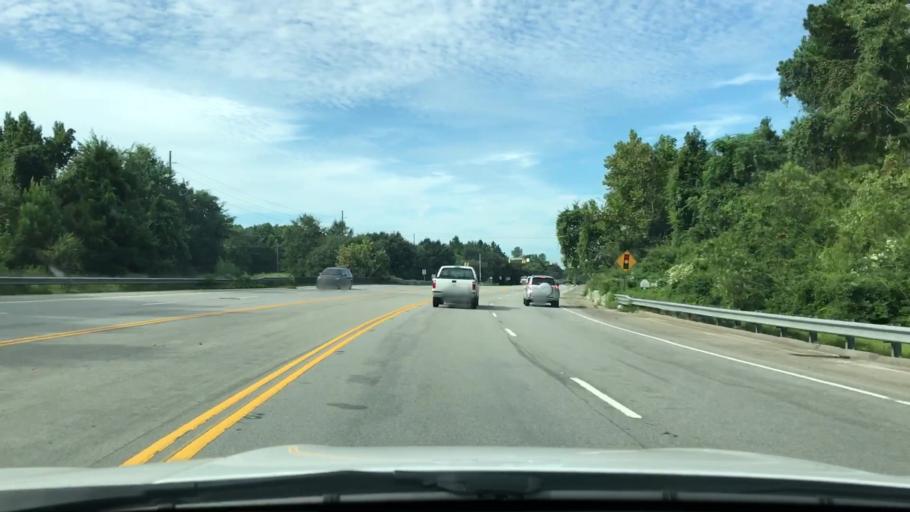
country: US
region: South Carolina
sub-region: Dorchester County
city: Summerville
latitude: 33.0122
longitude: -80.1750
